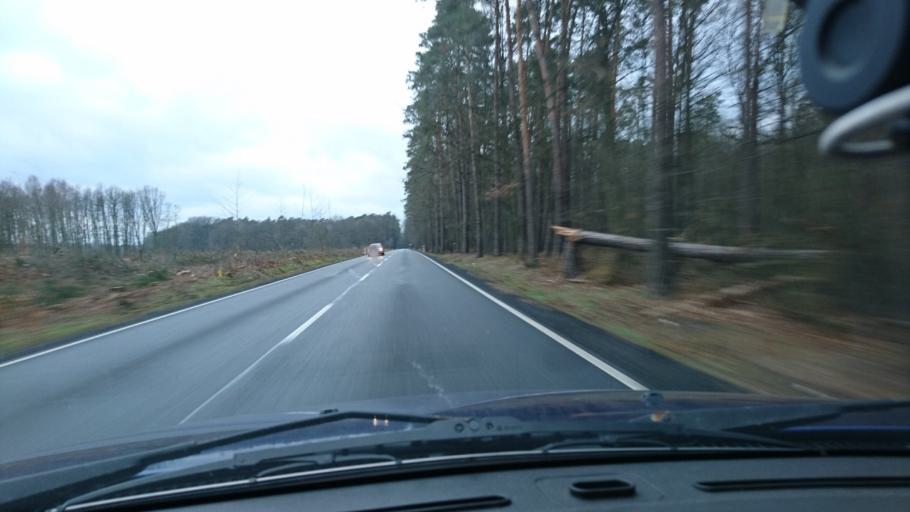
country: PL
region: Opole Voivodeship
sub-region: Powiat kluczborski
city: Kluczbork
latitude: 50.9400
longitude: 18.3266
